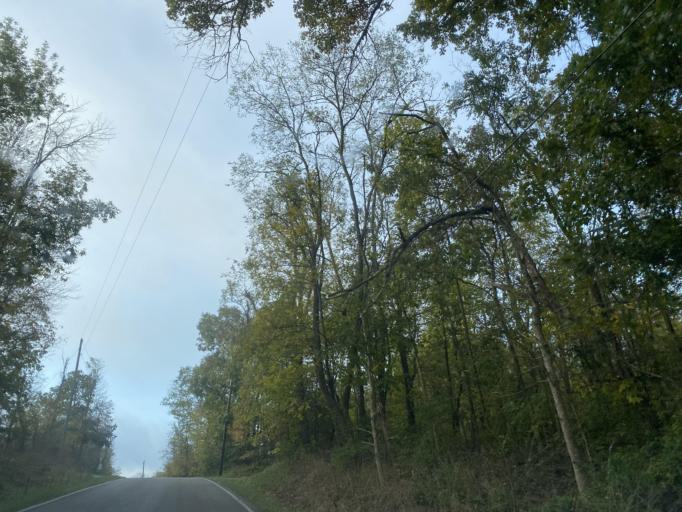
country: US
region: Kentucky
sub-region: Pendleton County
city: Falmouth
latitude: 38.7378
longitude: -84.3167
